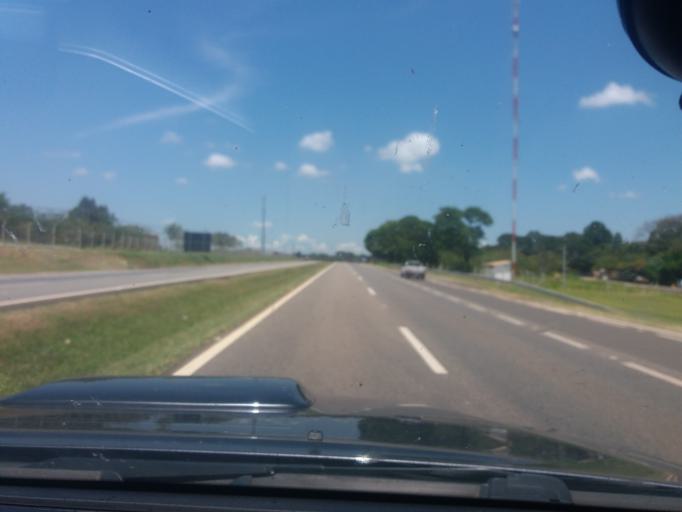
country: BR
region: Sao Paulo
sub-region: Tatui
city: Tatui
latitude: -23.3601
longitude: -47.8903
